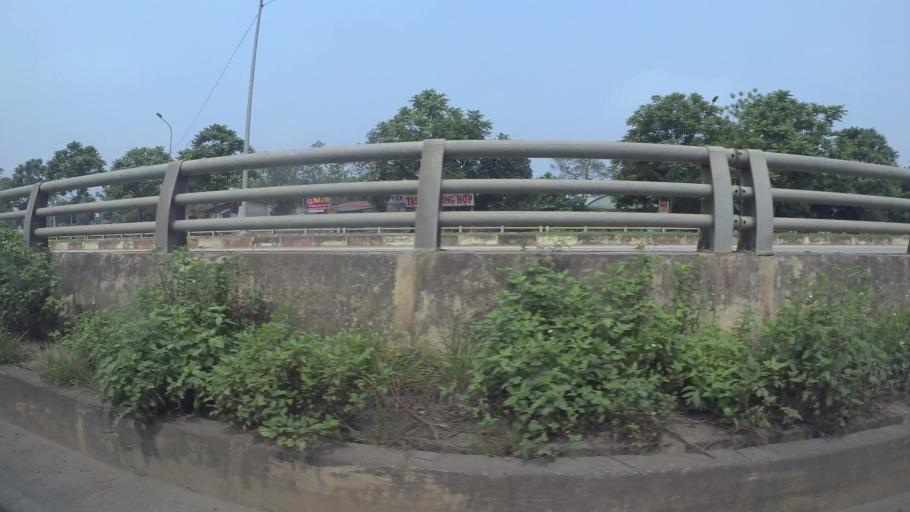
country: VN
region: Ha Noi
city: Lien Quan
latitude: 20.9886
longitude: 105.5365
